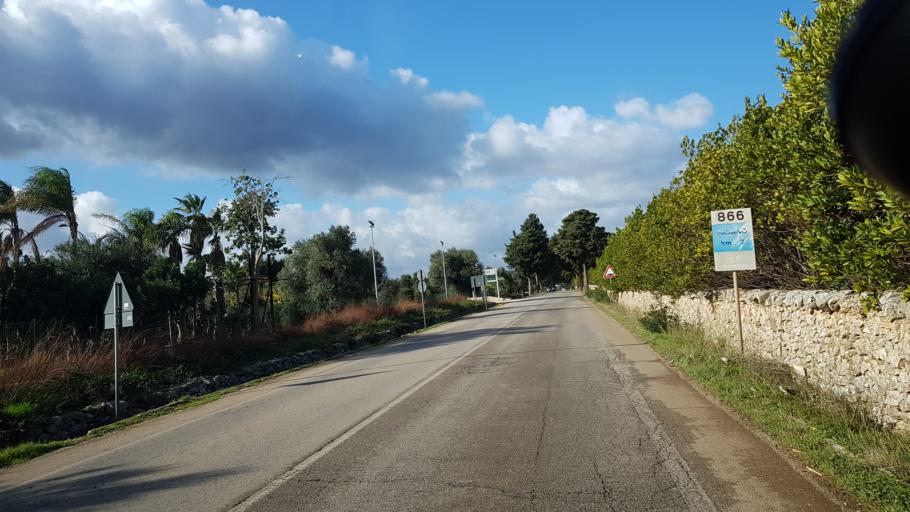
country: IT
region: Apulia
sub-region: Provincia di Brindisi
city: Pezze di Greco
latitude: 40.8003
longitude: 17.4406
